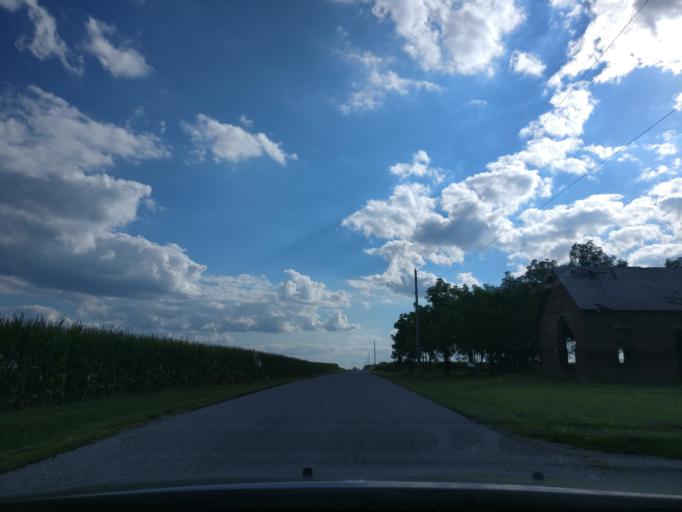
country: US
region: Ohio
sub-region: Clinton County
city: Wilmington
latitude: 39.5259
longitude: -83.7708
